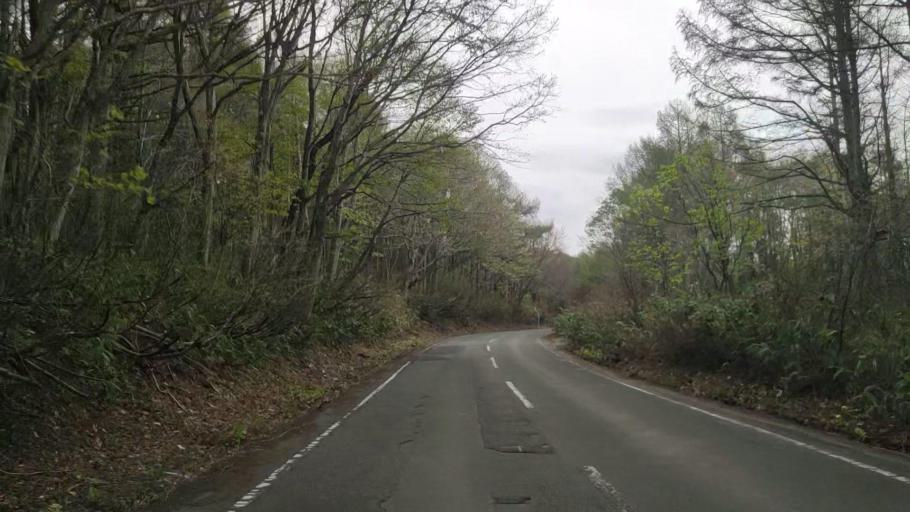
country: JP
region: Aomori
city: Aomori Shi
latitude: 40.7311
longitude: 140.8427
